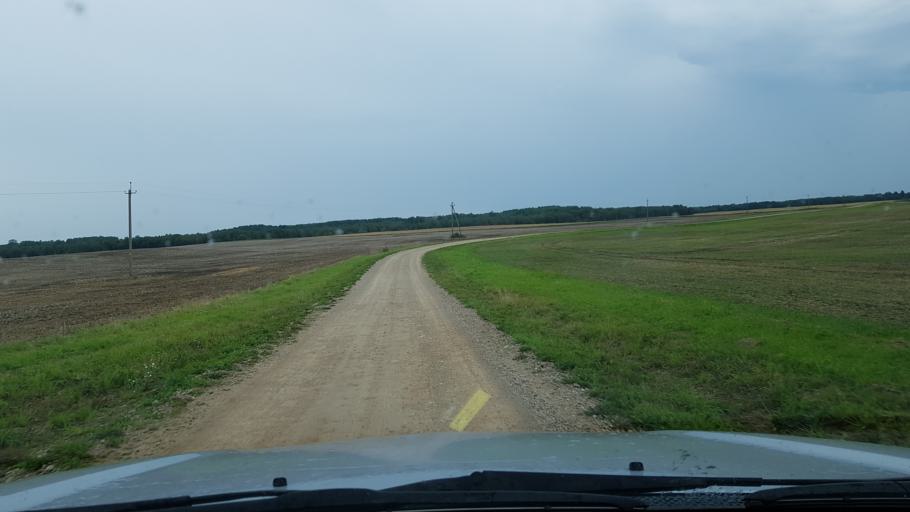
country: EE
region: Harju
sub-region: Rae vald
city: Jueri
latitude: 59.3372
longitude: 24.9284
